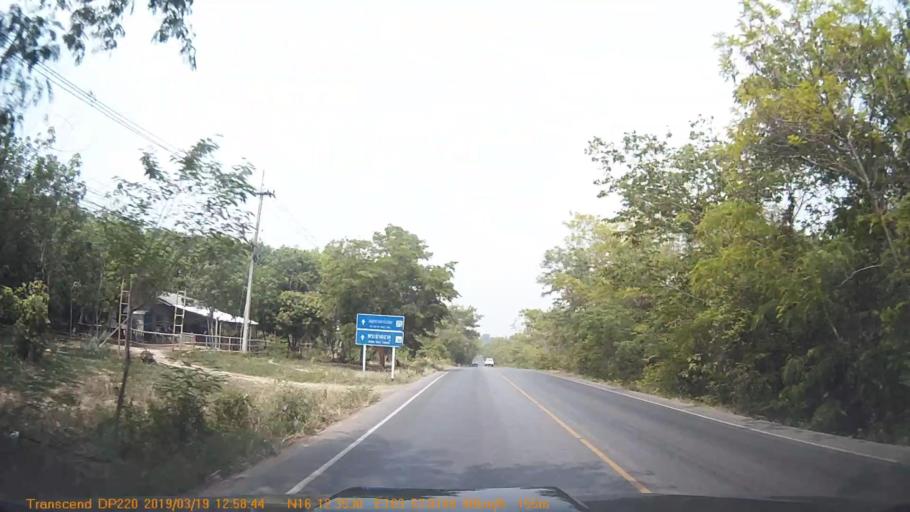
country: TH
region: Roi Et
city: Waeng
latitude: 16.2062
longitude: 103.9503
